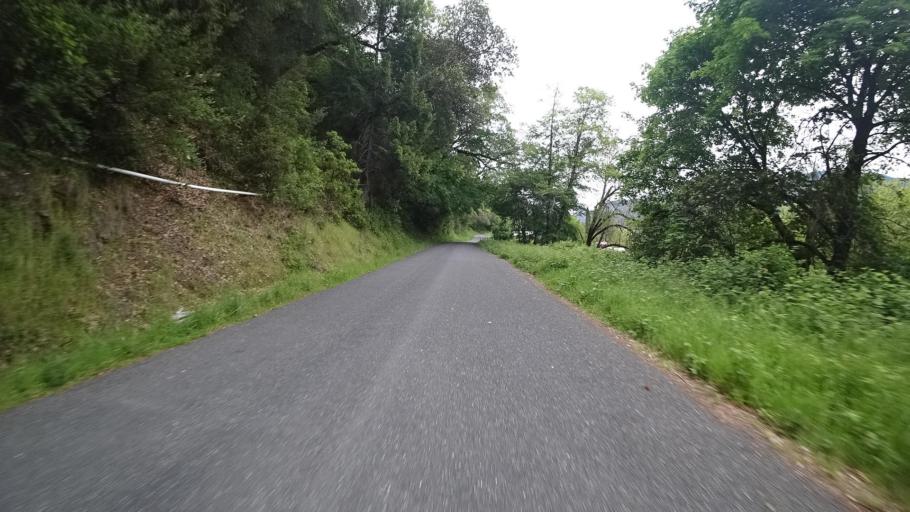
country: US
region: California
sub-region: Humboldt County
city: Willow Creek
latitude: 40.9454
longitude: -123.6111
